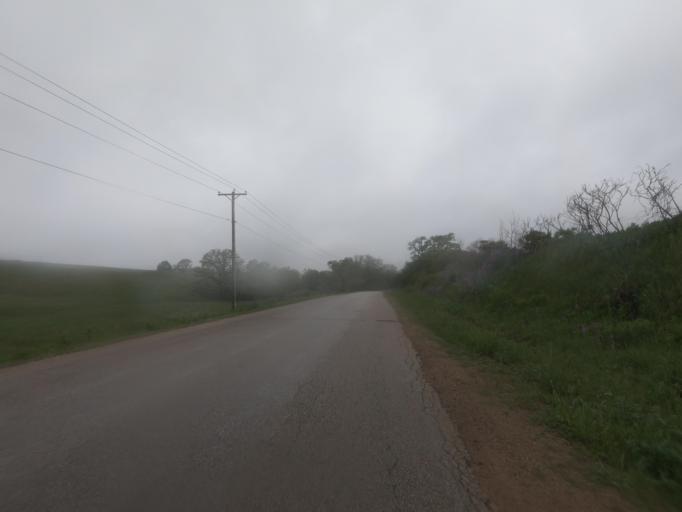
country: US
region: Wisconsin
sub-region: Grant County
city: Hazel Green
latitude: 42.5093
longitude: -90.4589
